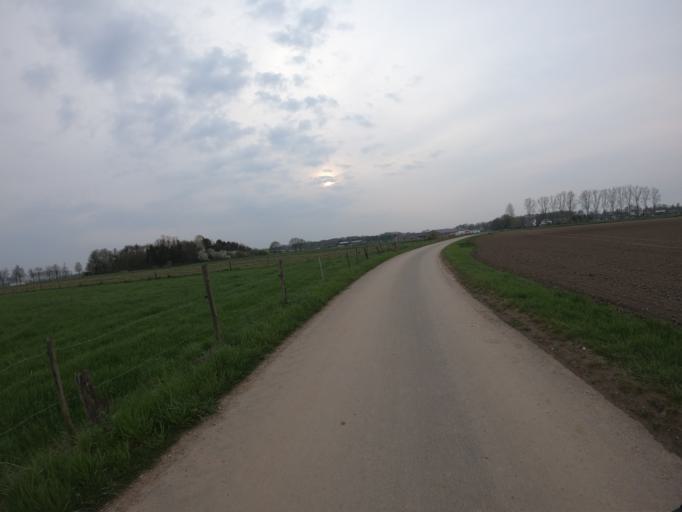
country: BE
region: Flanders
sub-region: Provincie Limburg
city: Maaseik
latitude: 51.0888
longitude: 5.7759
